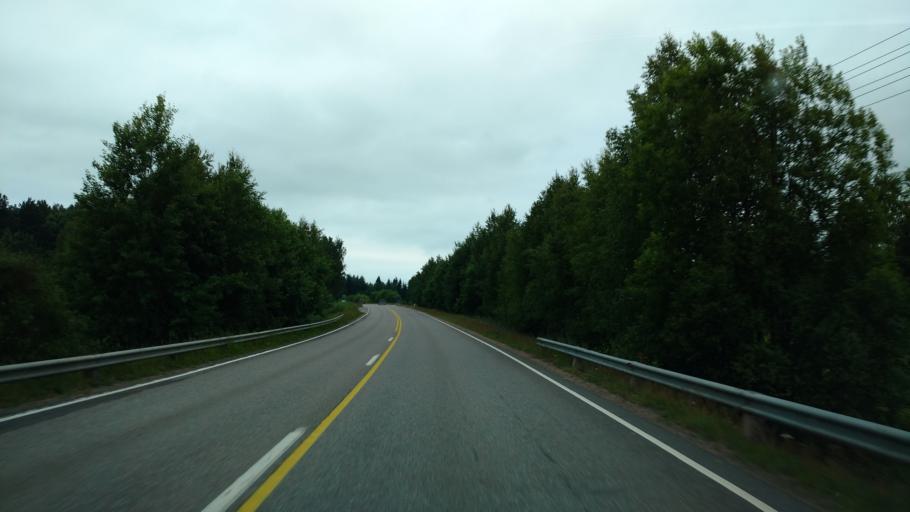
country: FI
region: Varsinais-Suomi
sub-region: Salo
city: Kiikala
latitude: 60.4092
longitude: 23.5855
